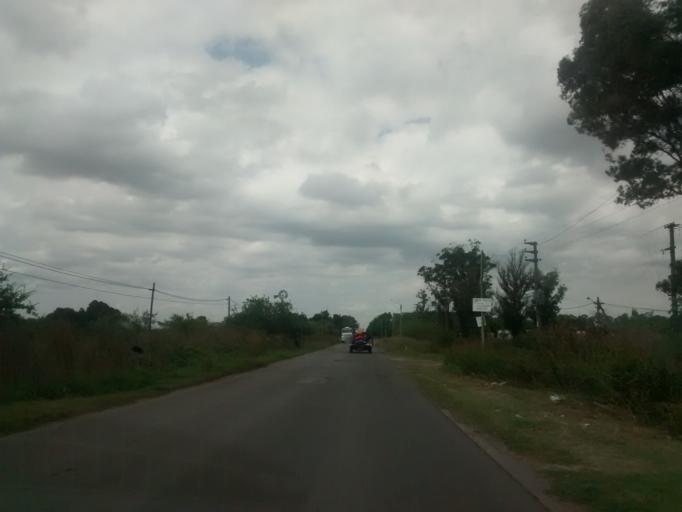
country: AR
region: Buenos Aires
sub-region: Partido de La Plata
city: La Plata
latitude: -34.9761
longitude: -57.9368
